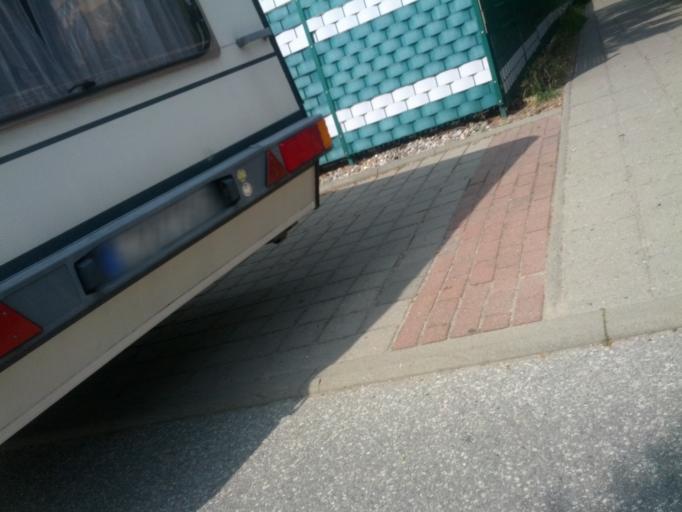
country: DE
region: Mecklenburg-Vorpommern
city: Bastorf
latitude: 54.1511
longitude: 11.7222
